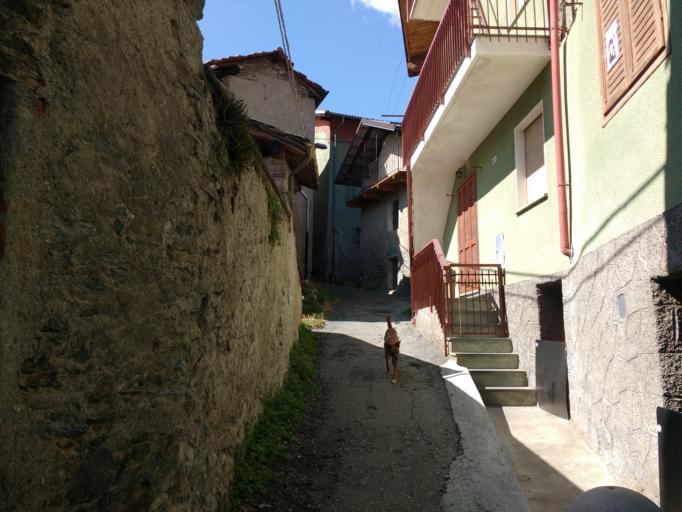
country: IT
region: Piedmont
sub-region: Provincia di Torino
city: Giaglione
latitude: 45.1407
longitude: 7.0080
